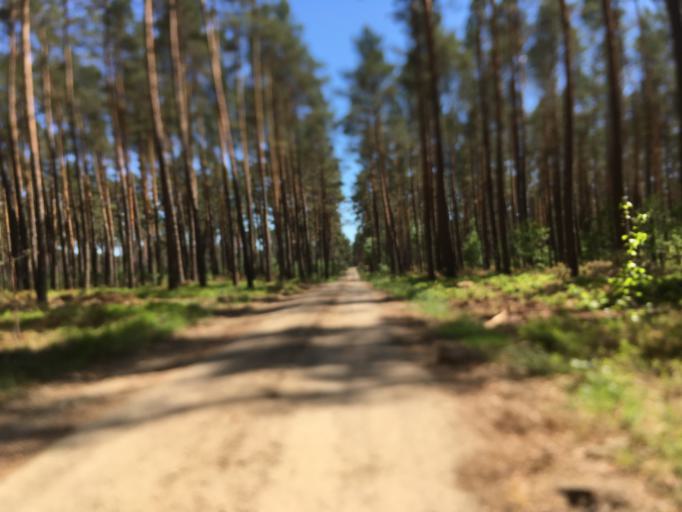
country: DE
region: Brandenburg
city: Friedrichswalde
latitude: 52.9761
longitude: 13.6312
